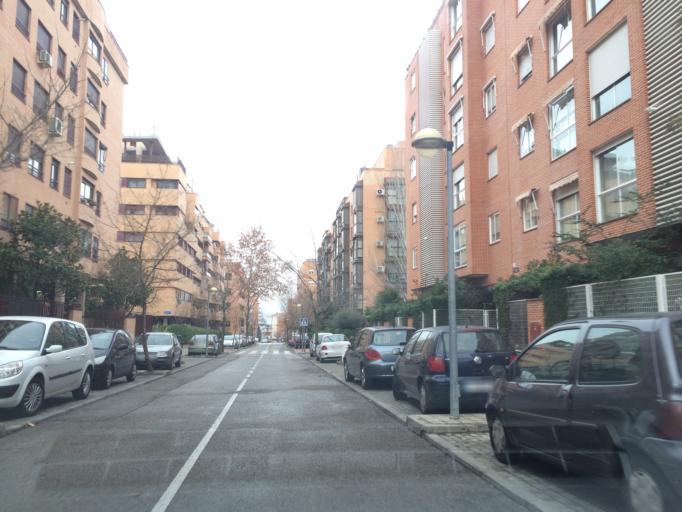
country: ES
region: Madrid
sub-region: Provincia de Madrid
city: Tres Cantos
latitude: 40.5970
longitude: -3.7138
